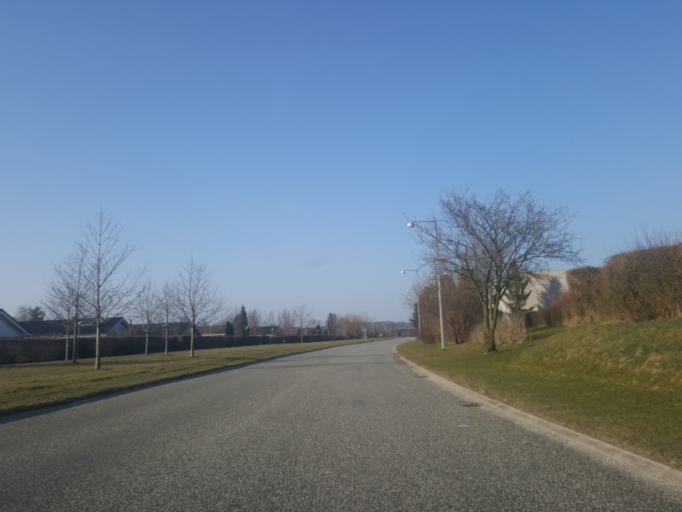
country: DK
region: Capital Region
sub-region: Allerod Kommune
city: Lillerod
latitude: 55.8693
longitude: 12.3283
